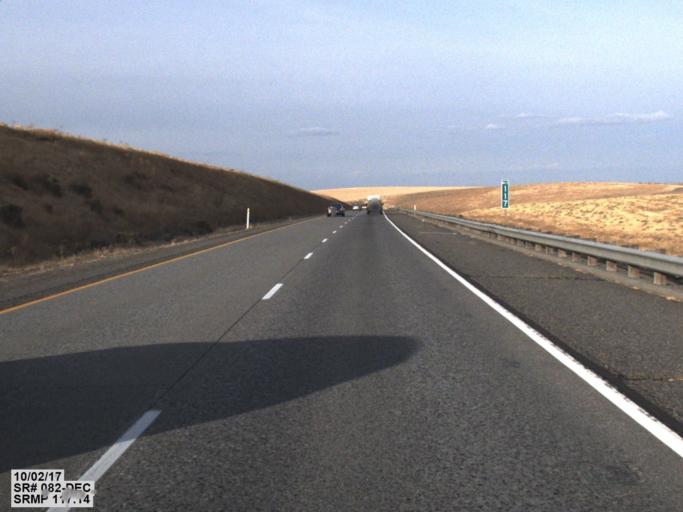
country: US
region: Washington
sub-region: Benton County
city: Highland
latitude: 46.1047
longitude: -119.2131
